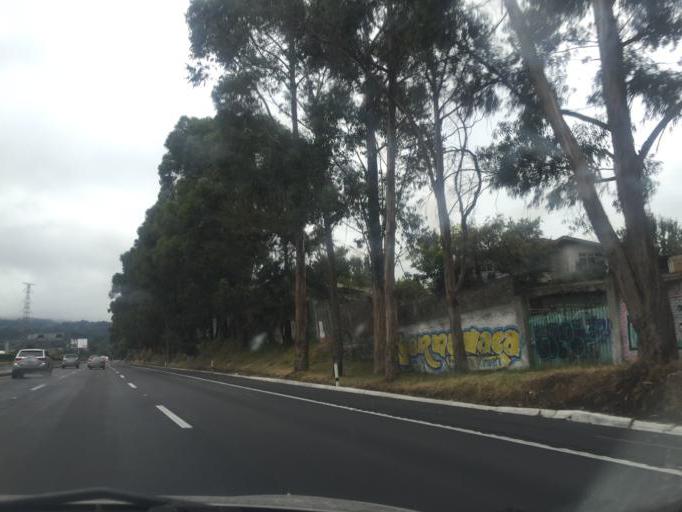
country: MX
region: Mexico City
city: Xochimilco
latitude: 19.1971
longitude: -99.1502
